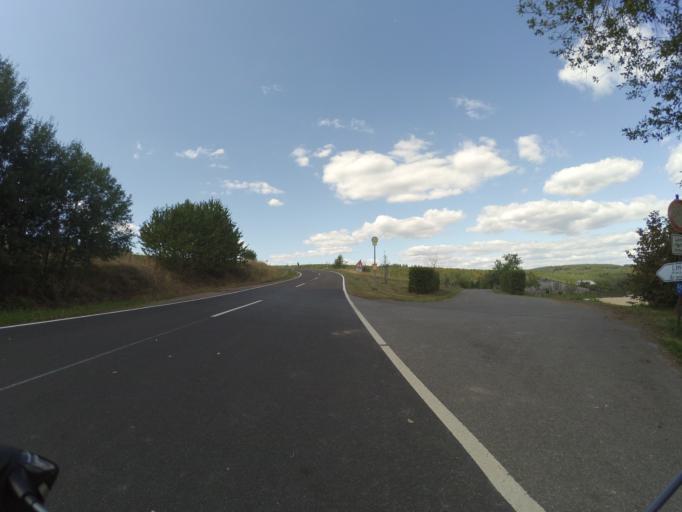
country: DE
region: Rheinland-Pfalz
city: Bescheid
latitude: 49.7608
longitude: 6.8782
